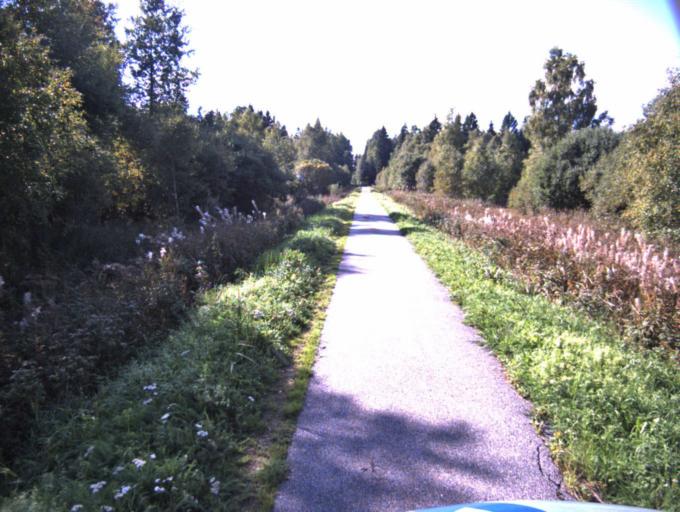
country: SE
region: Vaestra Goetaland
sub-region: Ulricehamns Kommun
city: Ulricehamn
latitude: 57.8362
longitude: 13.2459
